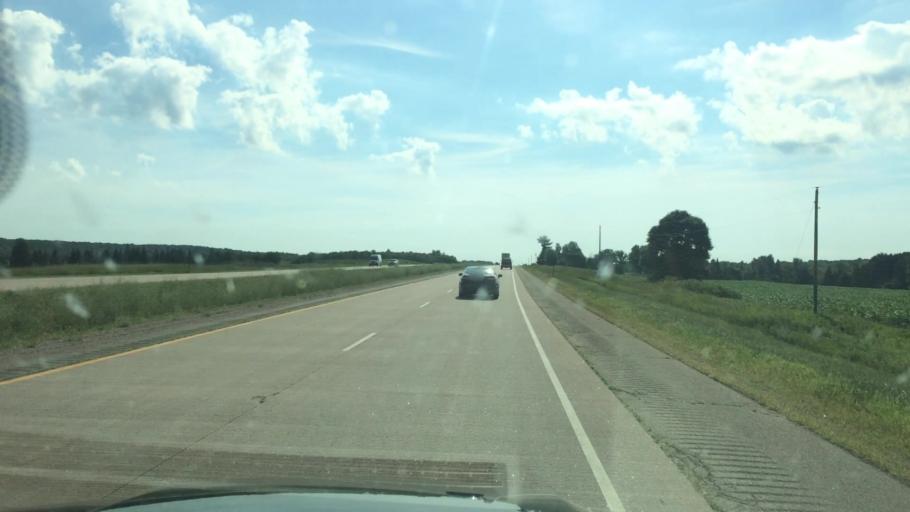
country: US
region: Wisconsin
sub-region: Shawano County
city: Wittenberg
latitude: 44.8039
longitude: -89.0064
